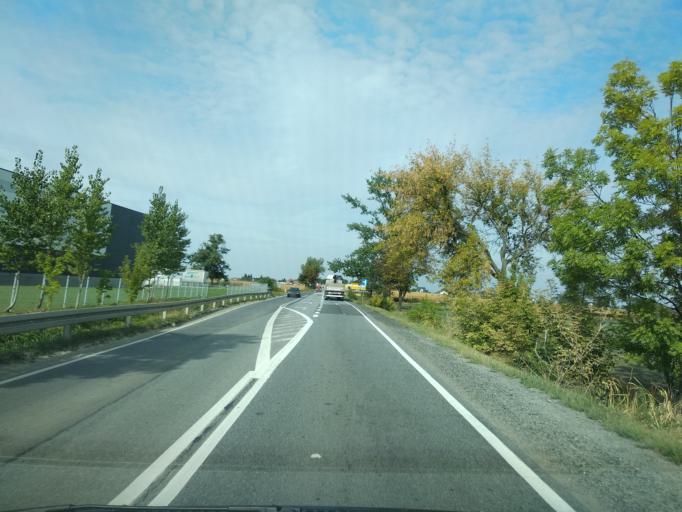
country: PL
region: Lower Silesian Voivodeship
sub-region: Powiat wroclawski
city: Zorawina
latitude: 50.9734
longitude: 17.0716
